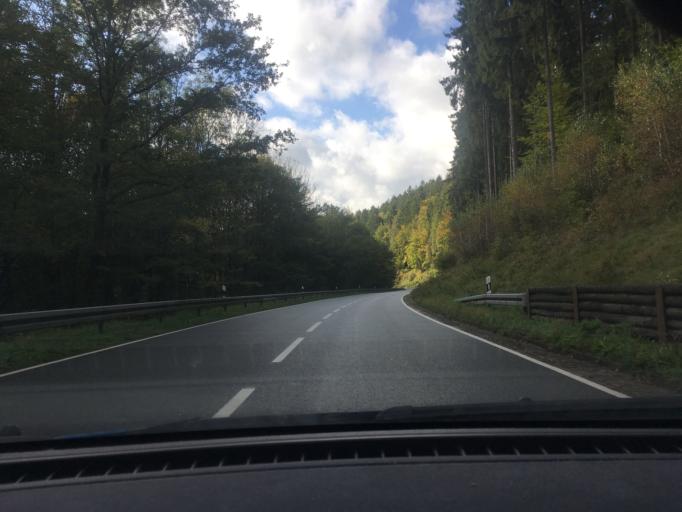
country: DE
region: Lower Saxony
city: Bevern
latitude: 51.7971
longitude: 9.5096
